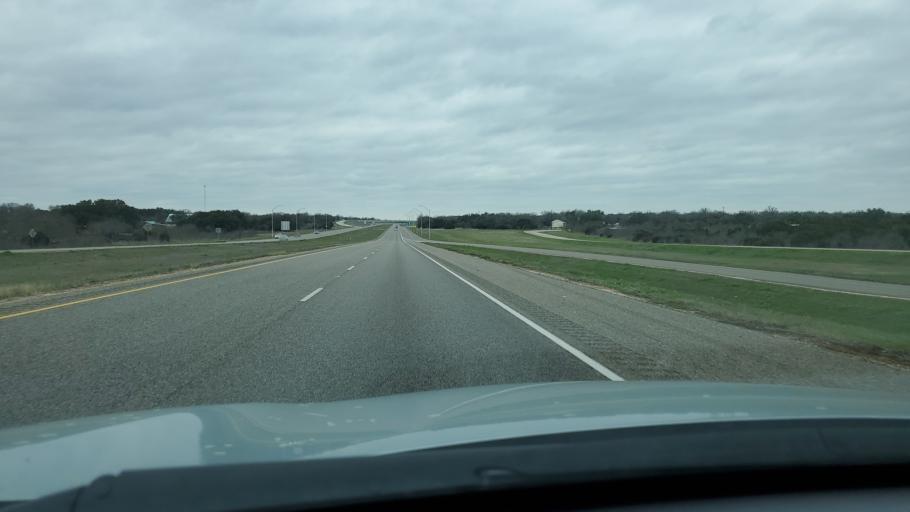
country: US
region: Texas
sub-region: Williamson County
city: Florence
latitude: 30.8458
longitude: -97.7869
